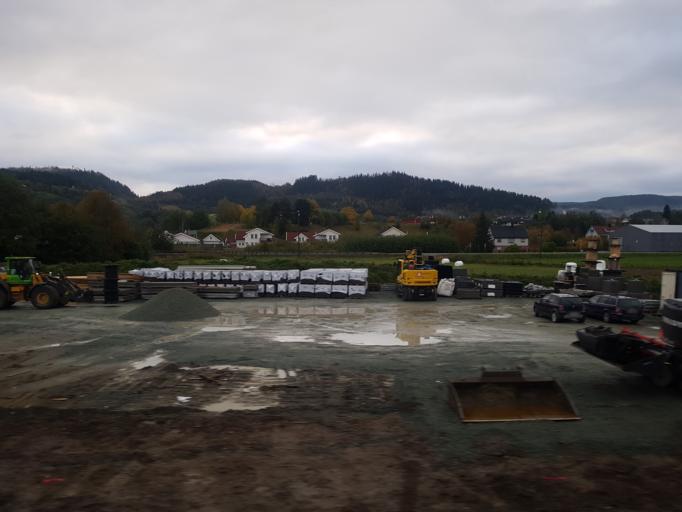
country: NO
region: Sor-Trondelag
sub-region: Melhus
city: Lundamo
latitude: 63.2064
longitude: 10.3041
